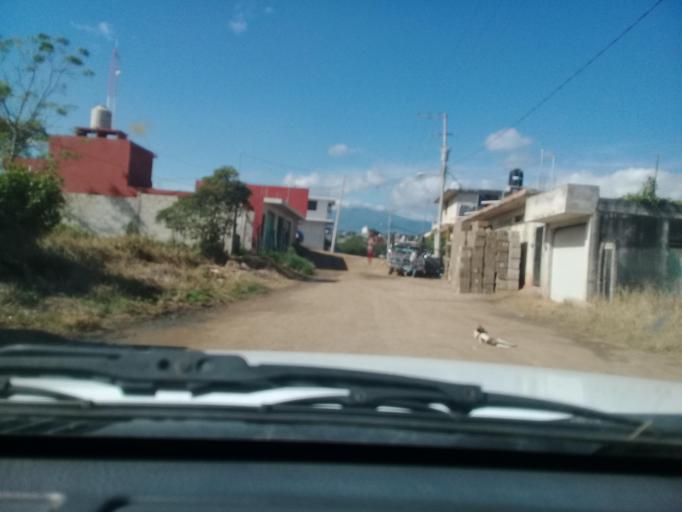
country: MX
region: Veracruz
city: El Castillo
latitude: 19.5649
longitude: -96.8810
